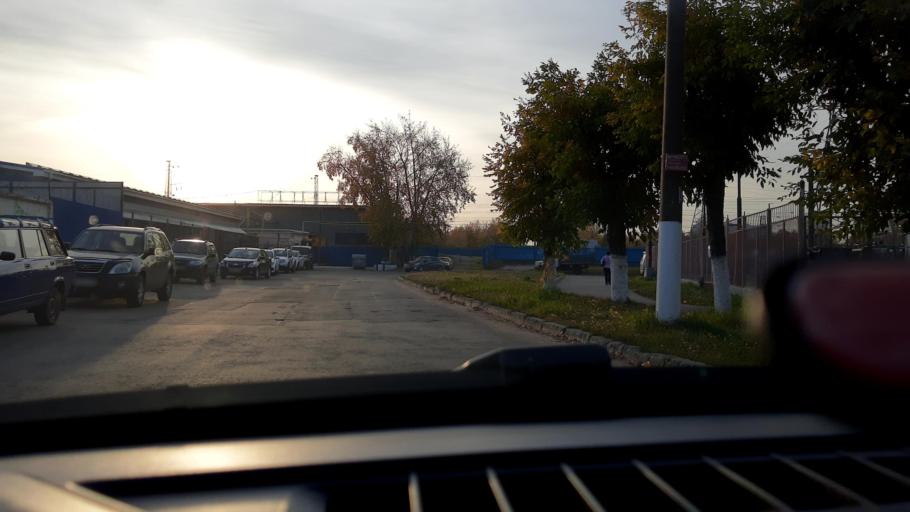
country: RU
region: Nizjnij Novgorod
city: Nizhniy Novgorod
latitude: 56.3123
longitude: 43.9167
